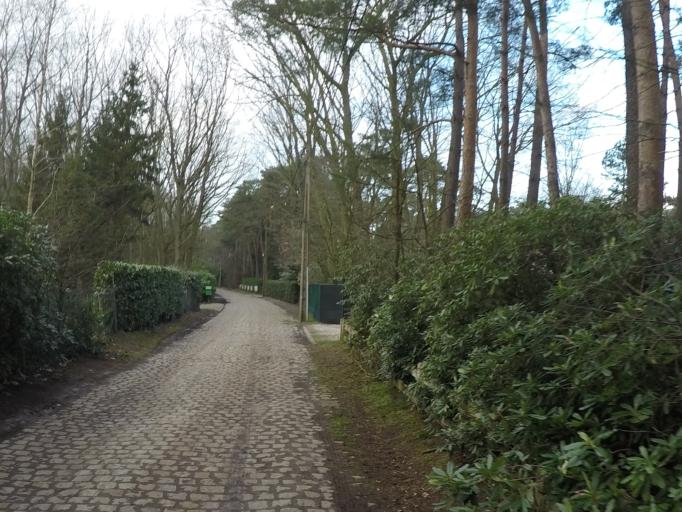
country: BE
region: Flanders
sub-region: Provincie Antwerpen
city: Stabroek
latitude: 51.3549
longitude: 4.3640
